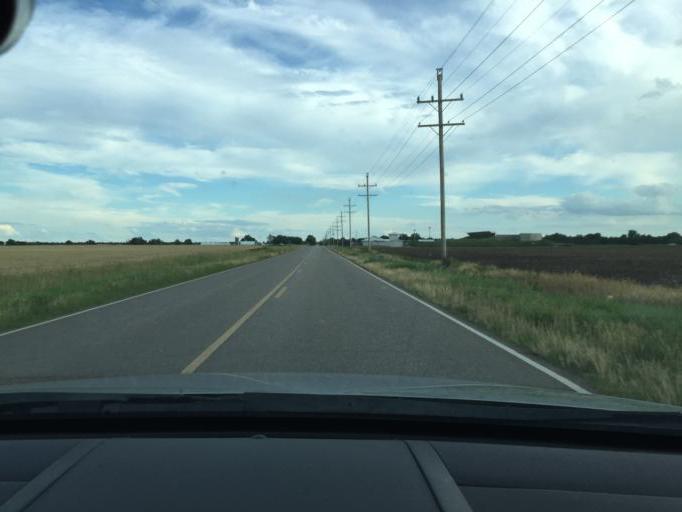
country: US
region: Kansas
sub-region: Reno County
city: South Hutchinson
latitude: 37.9398
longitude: -97.8852
